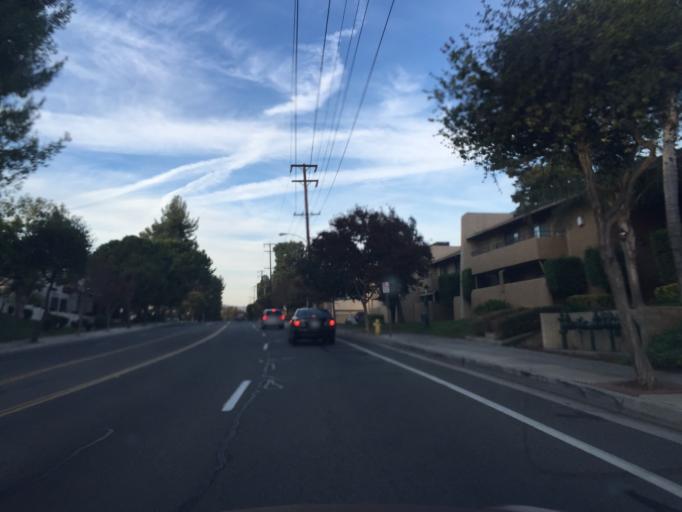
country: US
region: California
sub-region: Orange County
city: Brea
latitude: 33.8992
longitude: -117.8830
